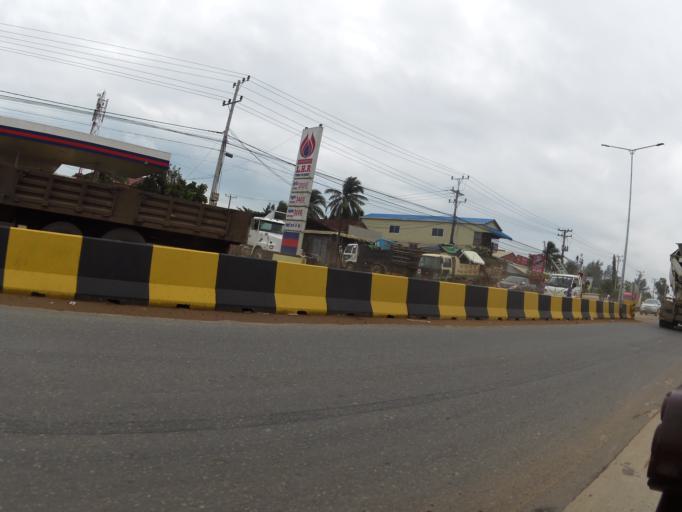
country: KH
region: Preah Sihanouk
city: Sihanoukville
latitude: 10.6379
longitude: 103.5317
